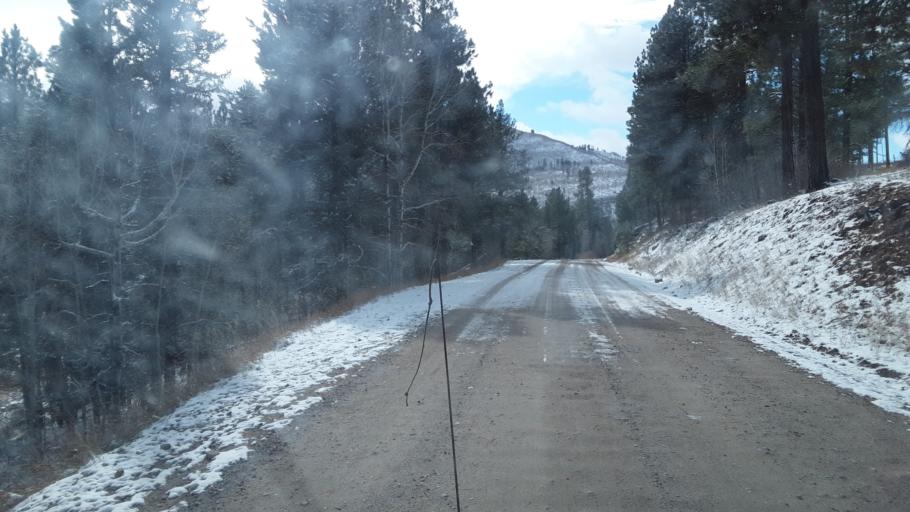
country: US
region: Colorado
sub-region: La Plata County
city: Bayfield
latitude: 37.4169
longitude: -107.5135
